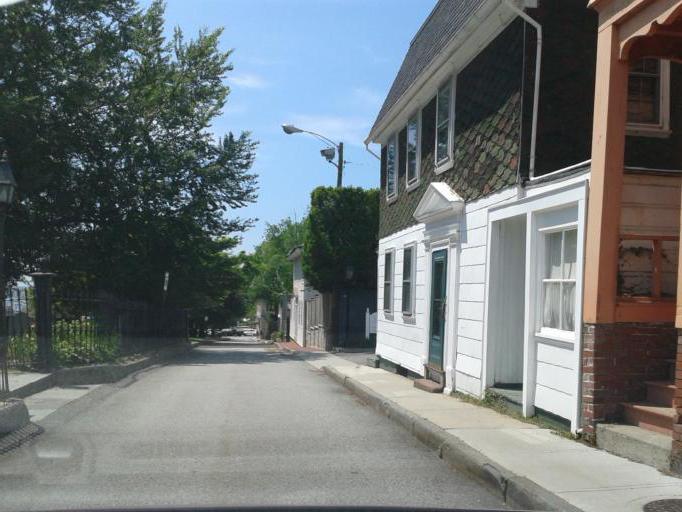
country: US
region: Rhode Island
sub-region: Newport County
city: Newport
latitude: 41.4874
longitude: -71.3130
